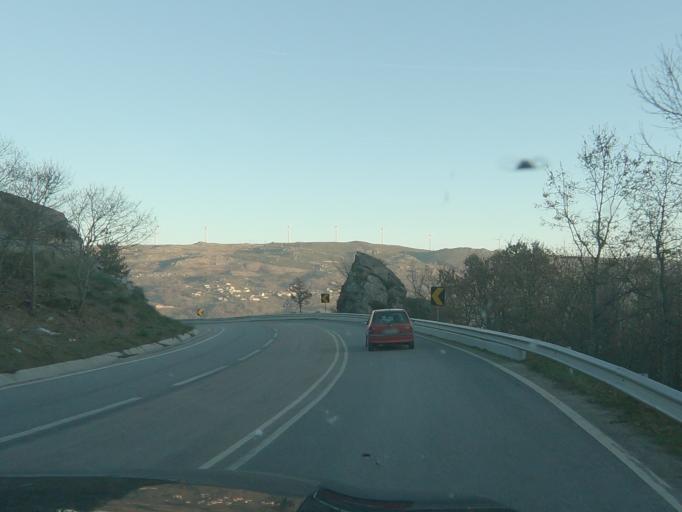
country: PT
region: Vila Real
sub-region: Vila Pouca de Aguiar
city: Vila Pouca de Aguiar
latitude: 41.4880
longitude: -7.6647
